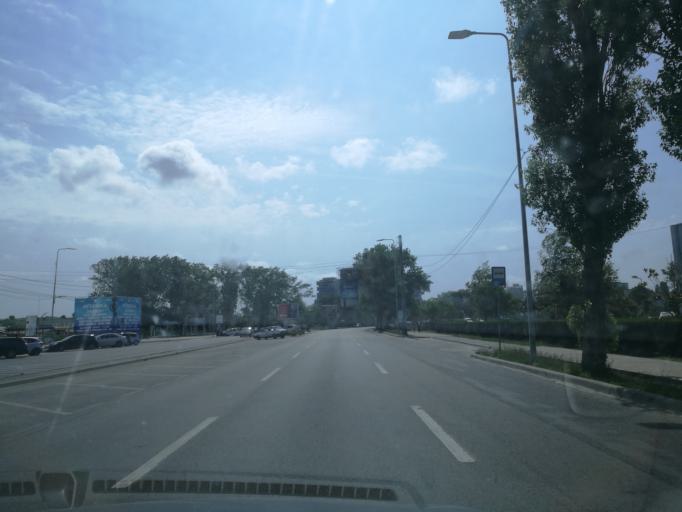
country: RO
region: Constanta
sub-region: Municipiul Constanta
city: Constanta
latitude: 44.2171
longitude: 28.6389
